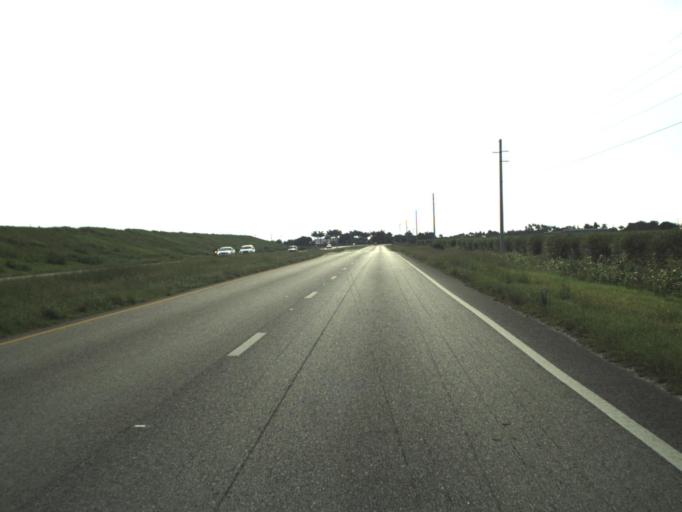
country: US
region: Florida
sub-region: Palm Beach County
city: South Bay
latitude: 26.6805
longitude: -80.7395
